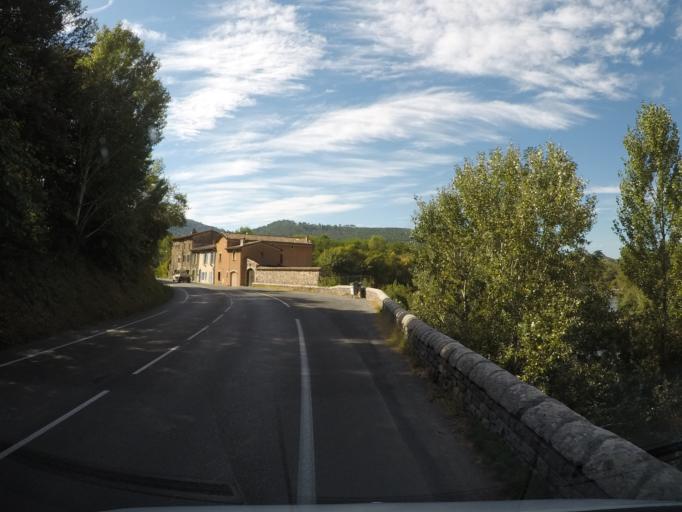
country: FR
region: Languedoc-Roussillon
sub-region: Departement du Gard
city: Anduze
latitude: 44.0601
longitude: 3.9822
